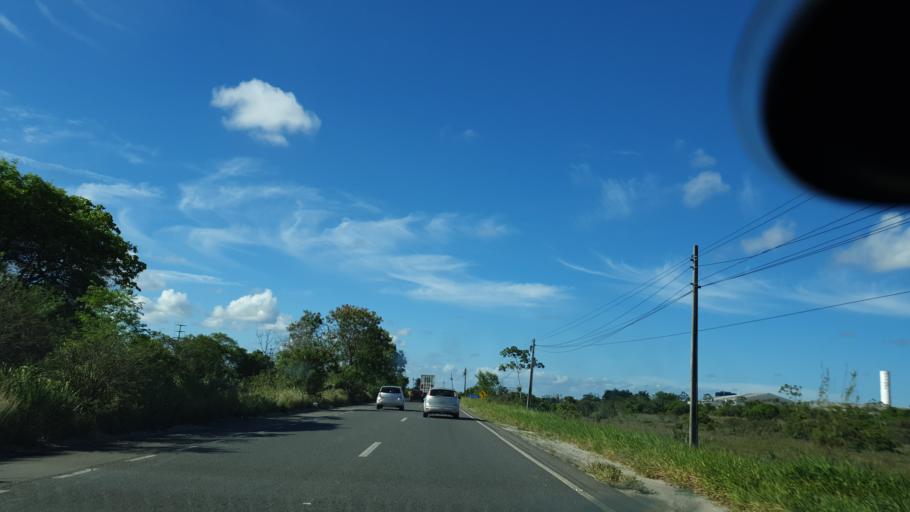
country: BR
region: Bahia
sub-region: Camacari
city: Camacari
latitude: -12.6696
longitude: -38.2999
